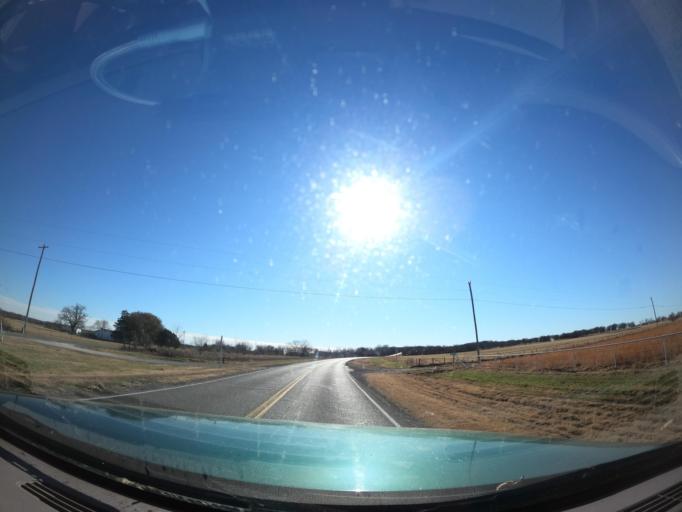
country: US
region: Oklahoma
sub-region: Muskogee County
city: Haskell
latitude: 35.6672
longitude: -95.6421
